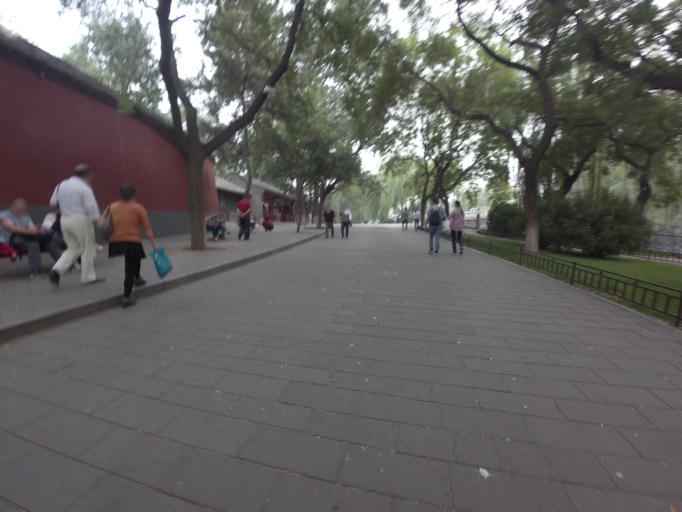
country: CN
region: Beijing
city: Jingshan
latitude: 39.9249
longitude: 116.3848
